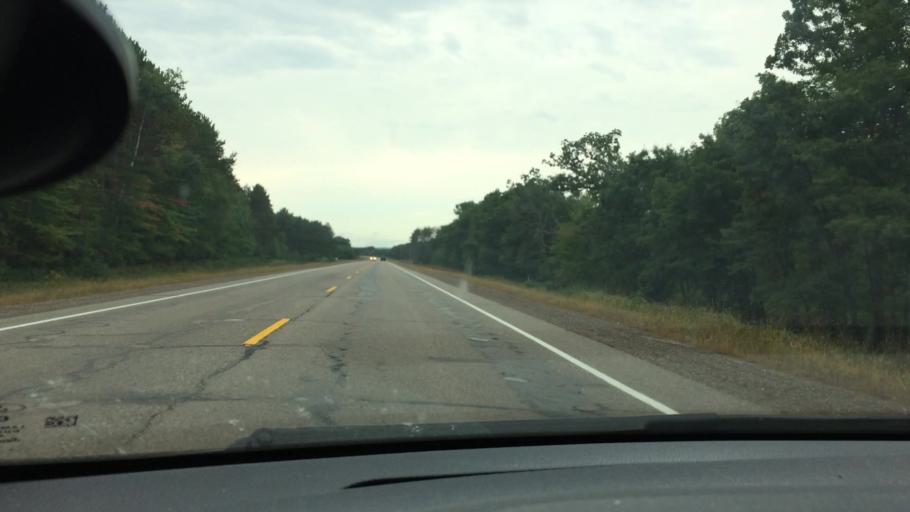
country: US
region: Wisconsin
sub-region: Eau Claire County
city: Augusta
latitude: 44.5821
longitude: -91.0846
